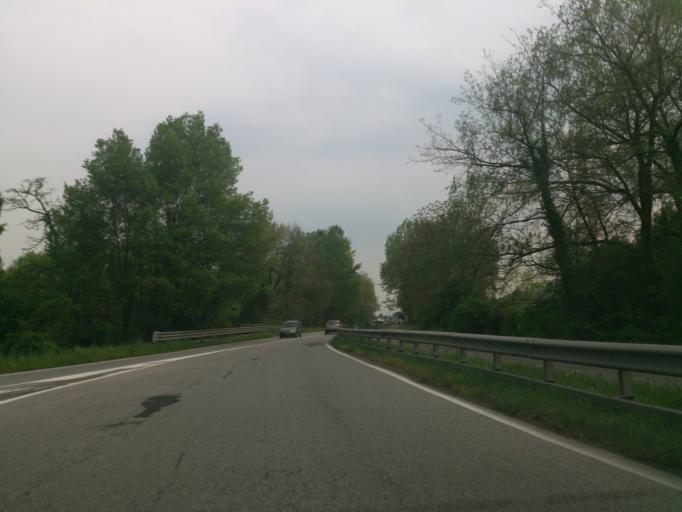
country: IT
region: Lombardy
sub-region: Citta metropolitana di Milano
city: Mezzate
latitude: 45.4498
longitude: 9.2879
